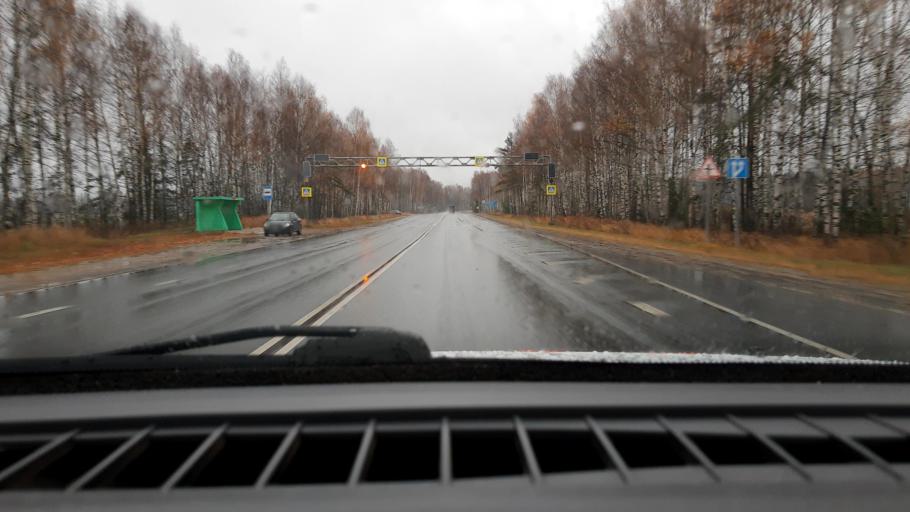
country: RU
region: Nizjnij Novgorod
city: Linda
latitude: 56.6531
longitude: 44.1189
